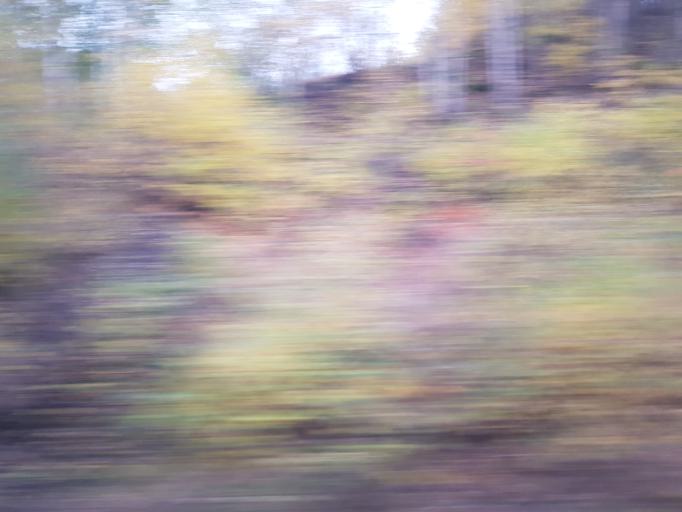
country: NO
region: Oppland
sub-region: Sel
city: Otta
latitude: 61.8436
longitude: 9.4059
